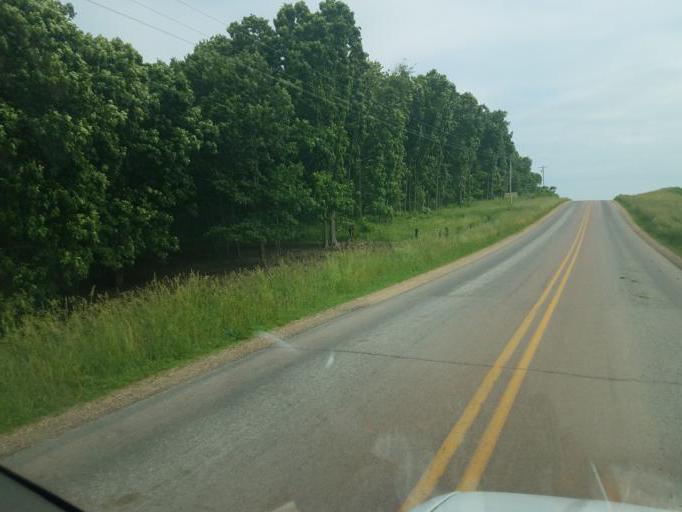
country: US
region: Wisconsin
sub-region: Vernon County
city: Hillsboro
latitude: 43.6418
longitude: -90.4526
